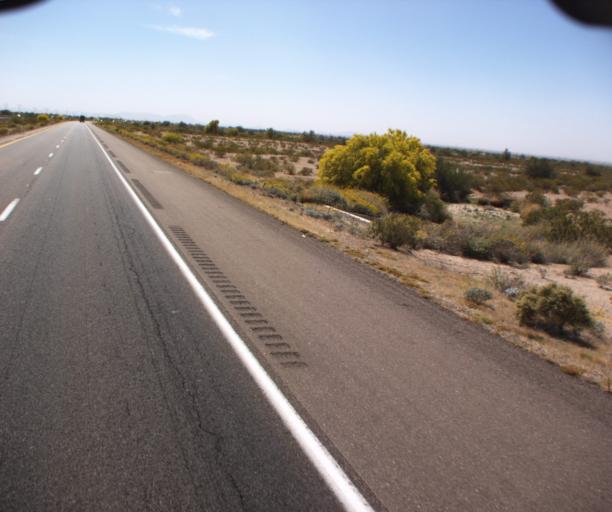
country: US
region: Arizona
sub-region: Maricopa County
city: Gila Bend
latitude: 33.0241
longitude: -112.6494
